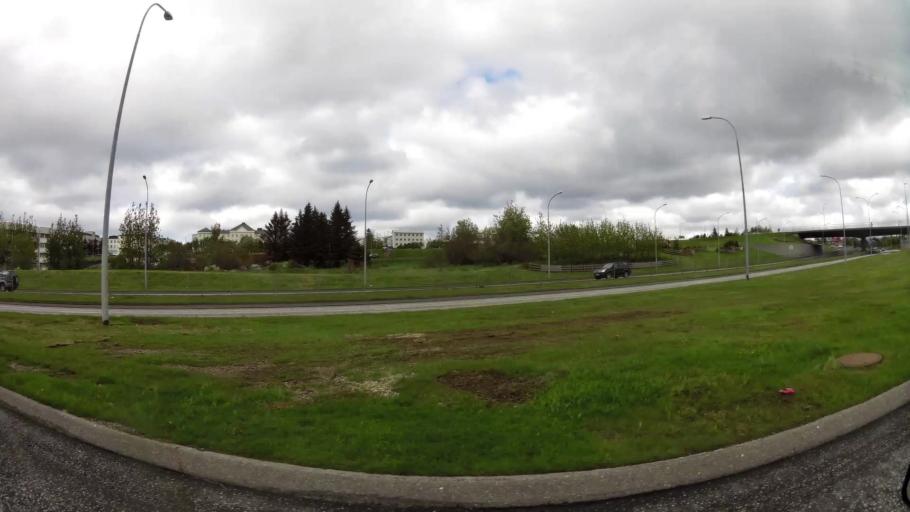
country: IS
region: Capital Region
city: Kopavogur
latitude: 64.1356
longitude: -21.9267
